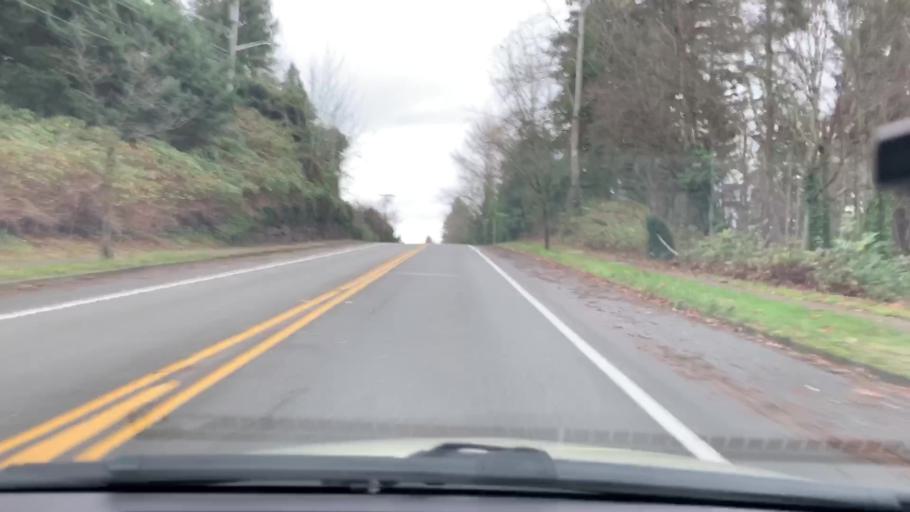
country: US
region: Washington
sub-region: King County
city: Kingsgate
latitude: 47.7183
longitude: -122.1846
